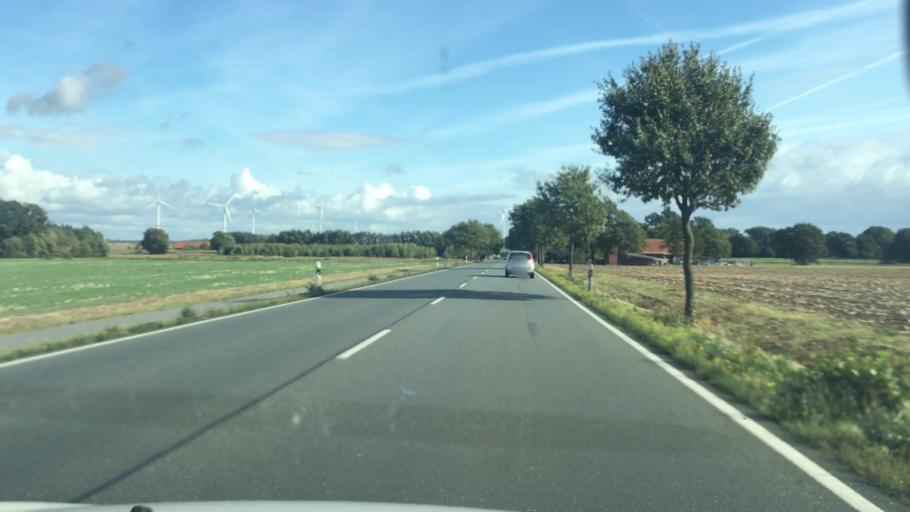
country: DE
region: Lower Saxony
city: Maasen
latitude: 52.6761
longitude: 8.9119
